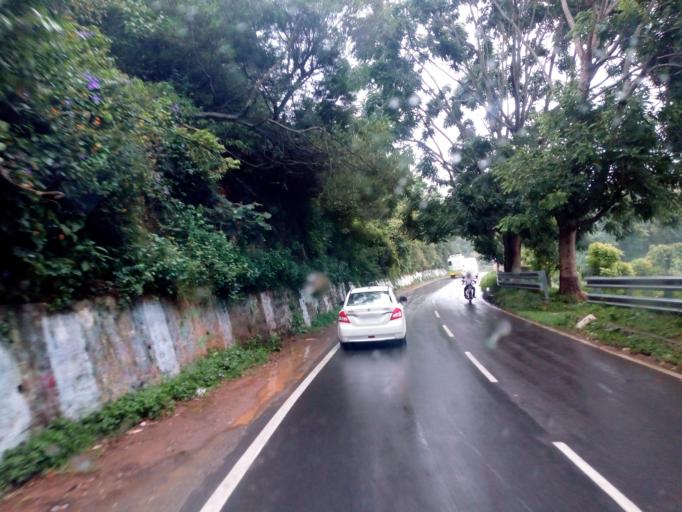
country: IN
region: Tamil Nadu
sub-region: Nilgiri
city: Wellington
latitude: 11.3497
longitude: 76.7853
